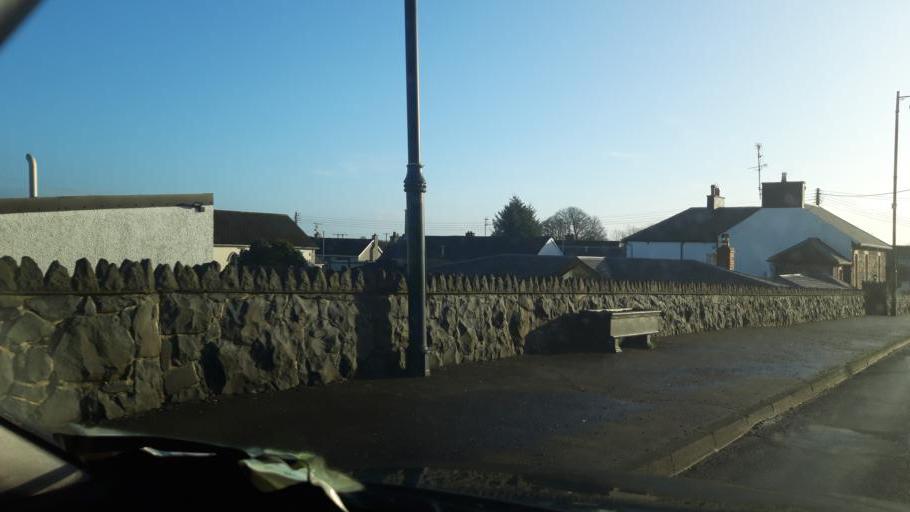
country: GB
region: Northern Ireland
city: Maghera
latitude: 54.9105
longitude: -6.6641
